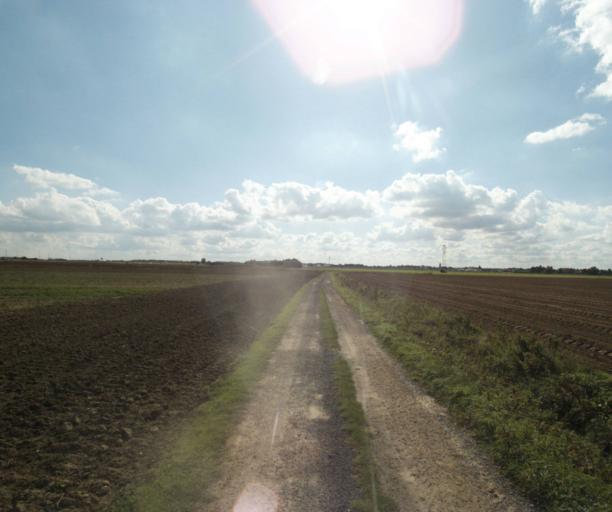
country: FR
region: Nord-Pas-de-Calais
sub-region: Departement du Nord
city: Illies
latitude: 50.5508
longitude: 2.8209
